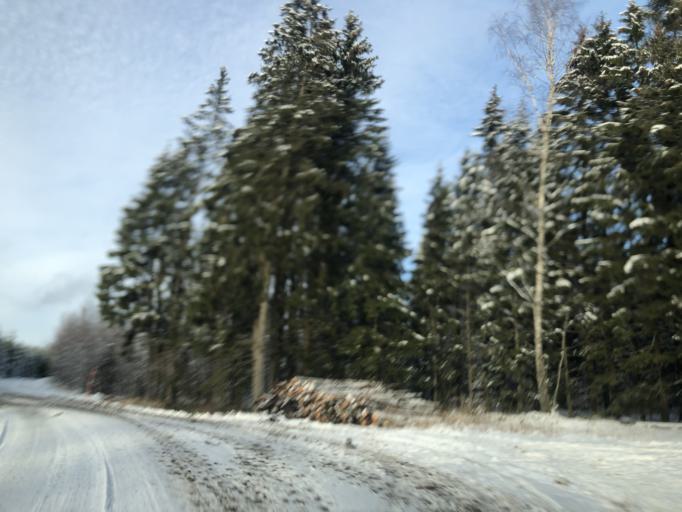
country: SE
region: Vaestra Goetaland
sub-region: Ulricehamns Kommun
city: Ulricehamn
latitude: 57.7582
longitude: 13.5185
